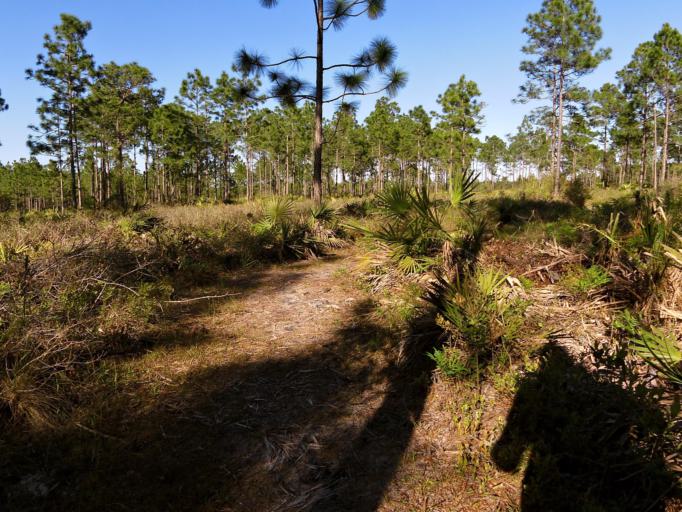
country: US
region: Florida
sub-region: Duval County
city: Atlantic Beach
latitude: 30.4770
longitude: -81.4914
